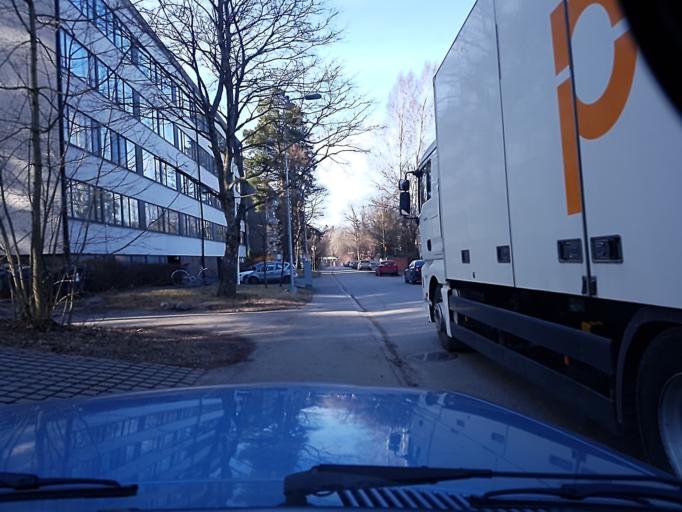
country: FI
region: Uusimaa
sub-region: Helsinki
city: Teekkarikylae
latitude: 60.1659
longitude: 24.8598
